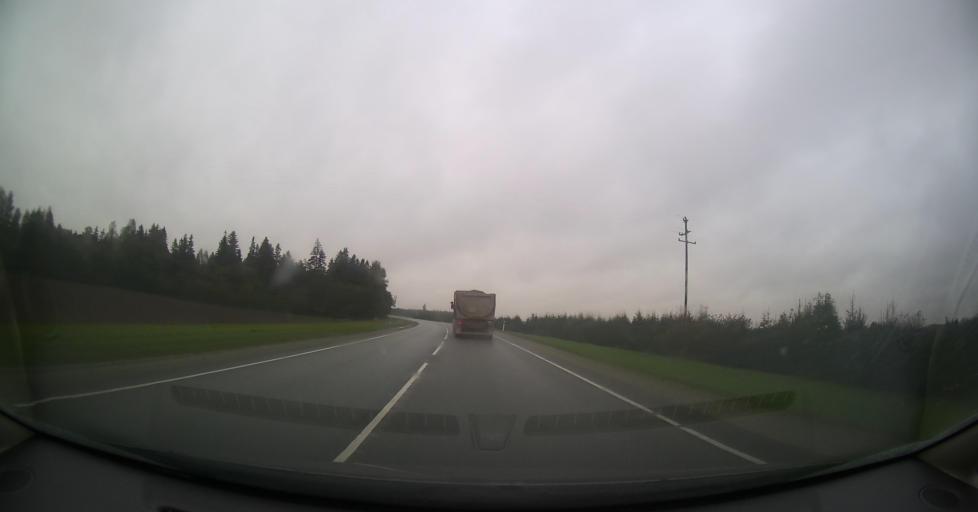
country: EE
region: Jaervamaa
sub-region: Paide linn
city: Paide
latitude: 59.0194
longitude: 25.5861
